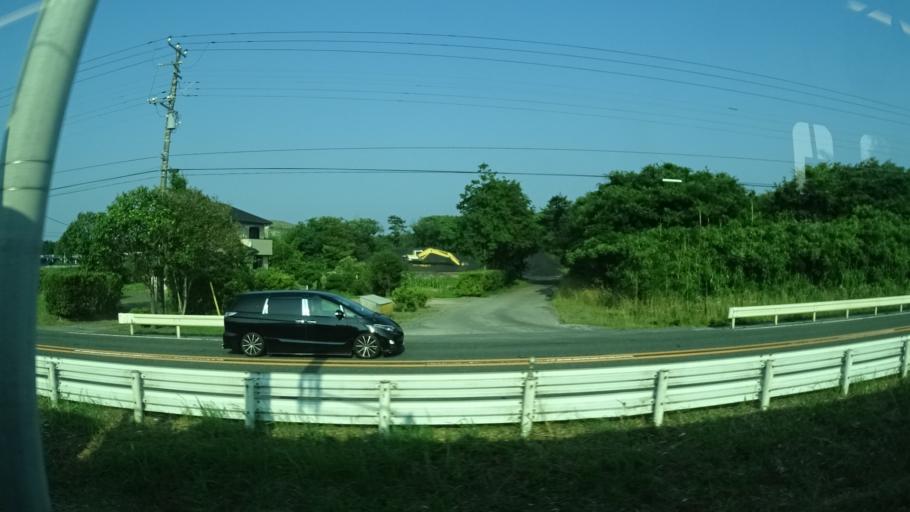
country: JP
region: Ibaraki
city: Kitaibaraki
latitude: 36.7715
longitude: 140.7391
